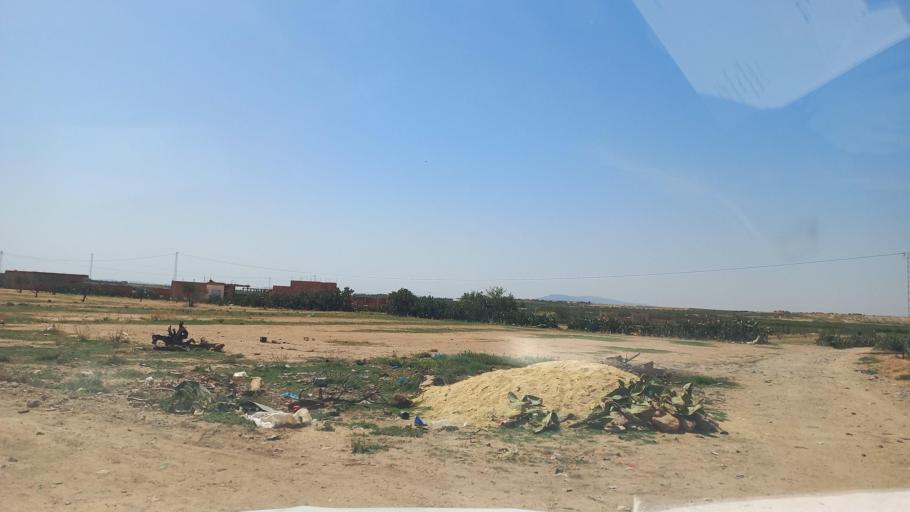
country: TN
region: Al Qasrayn
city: Sbiba
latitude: 35.3614
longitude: 9.0885
